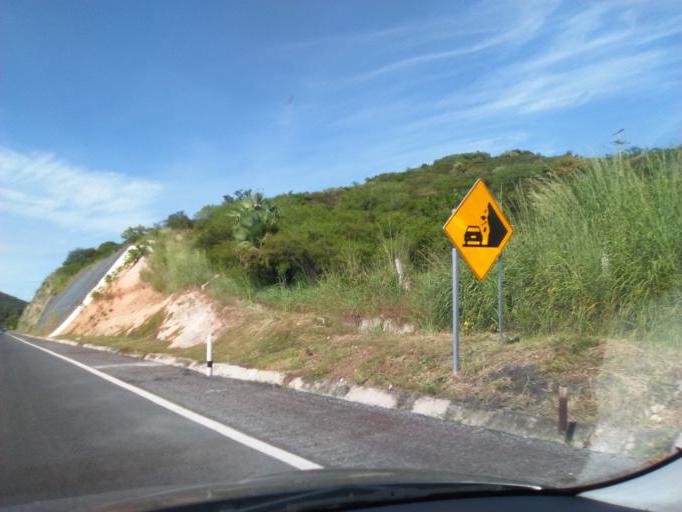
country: MX
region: Guerrero
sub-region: Huitzuco de los Figueroa
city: Ciudad de Huitzuco
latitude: 18.1503
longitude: -99.2124
